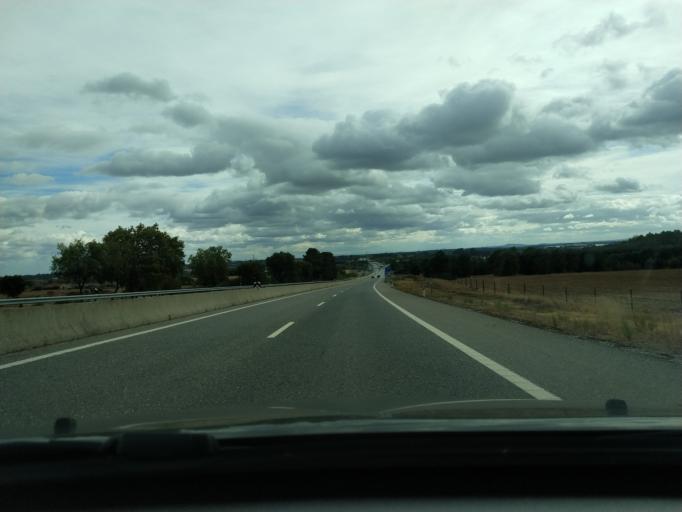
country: PT
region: Castelo Branco
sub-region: Concelho do Fundao
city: Fundao
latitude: 40.0424
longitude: -7.4702
